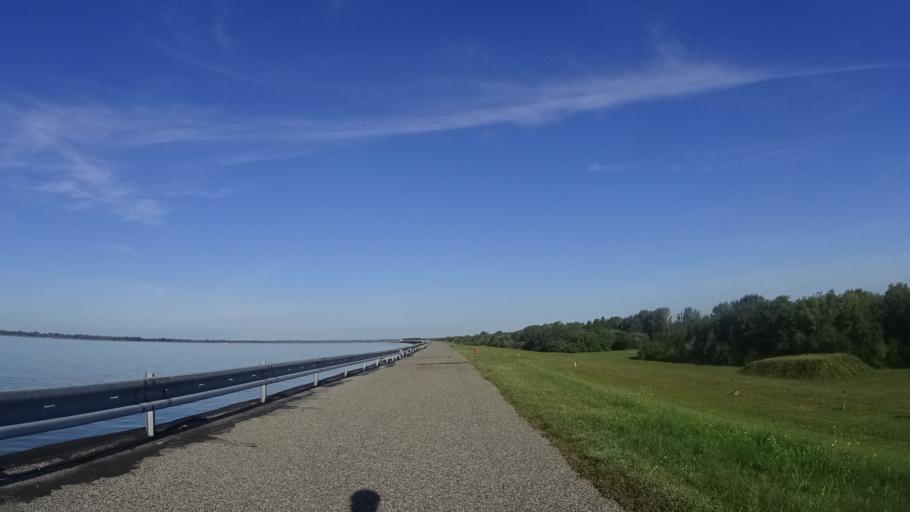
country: SK
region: Trnavsky
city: Samorin
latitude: 48.0056
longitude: 17.3330
